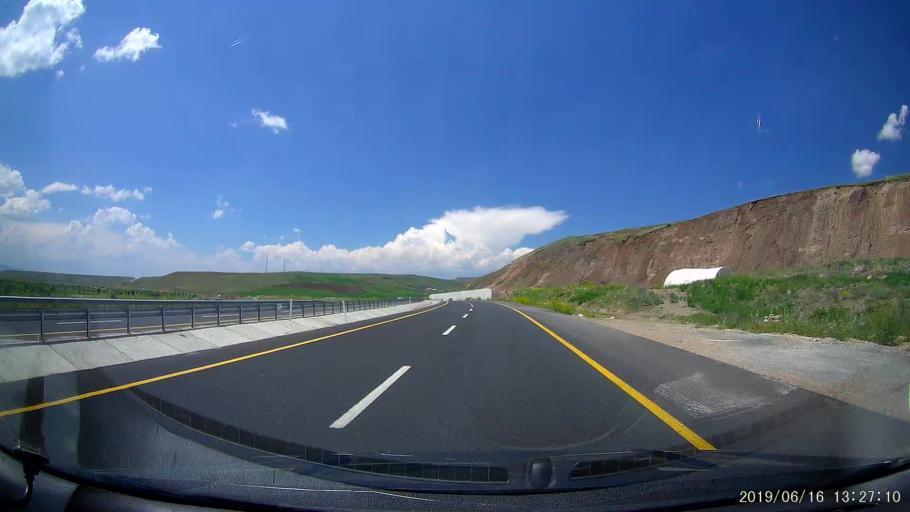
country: TR
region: Agri
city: Taslicay
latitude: 39.6678
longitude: 43.3151
